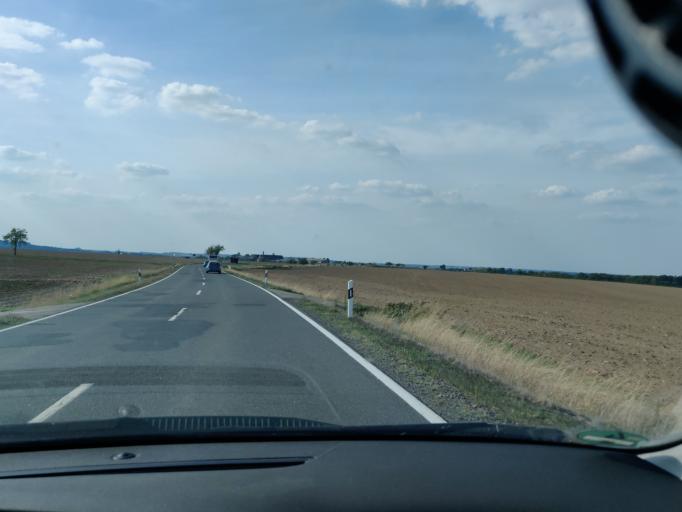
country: DE
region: Saxony
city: Seelitz
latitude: 51.0254
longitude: 12.8461
